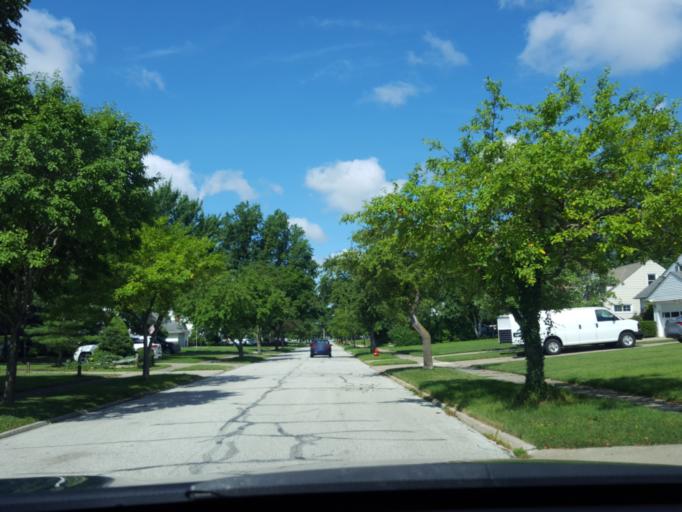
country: US
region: Ohio
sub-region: Cuyahoga County
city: Lyndhurst
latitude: 41.5238
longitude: -81.4928
